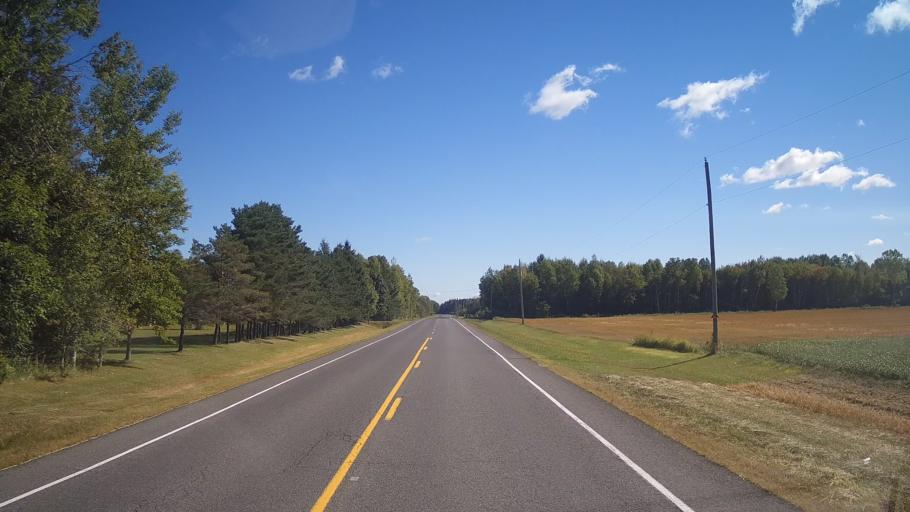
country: CA
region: Ontario
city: Prescott
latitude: 44.9136
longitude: -75.4207
